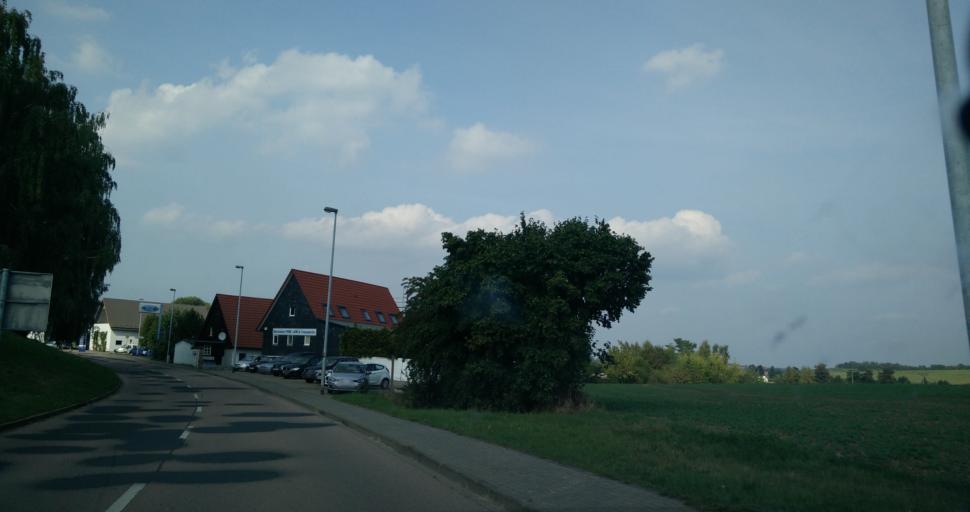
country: DE
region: Saxony
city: Rochlitz
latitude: 51.0590
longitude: 12.7891
